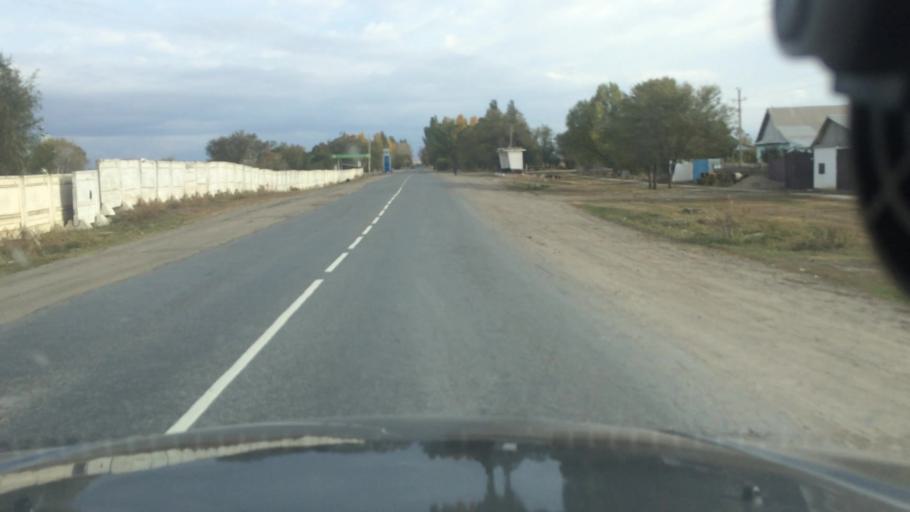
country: KG
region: Ysyk-Koel
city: Karakol
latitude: 42.5379
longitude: 78.3826
